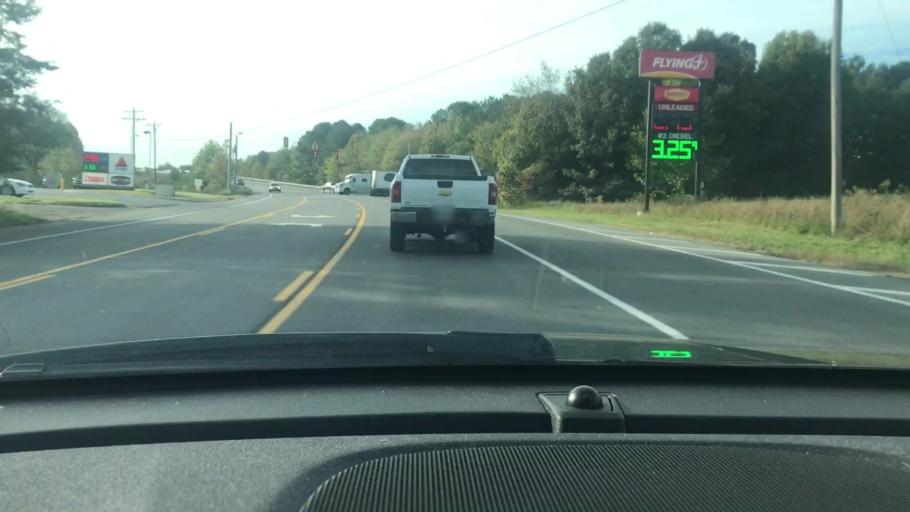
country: US
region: Tennessee
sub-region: Williamson County
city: Fairview
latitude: 36.0265
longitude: -87.1734
